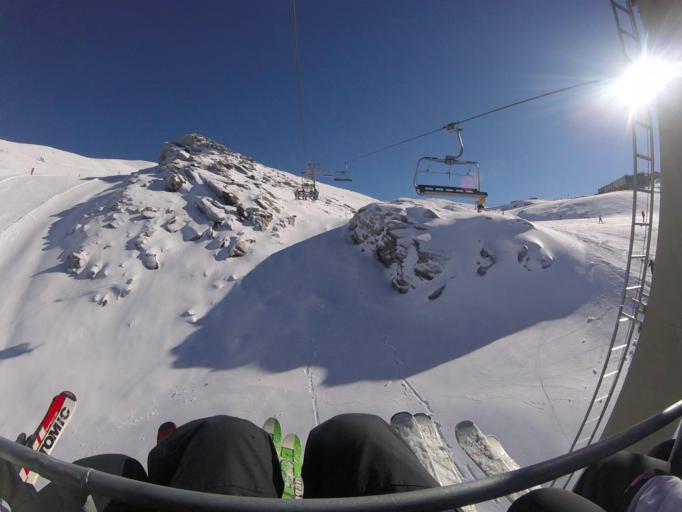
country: ES
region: Andalusia
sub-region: Provincia de Granada
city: Guejar-Sierra
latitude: 37.0752
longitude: -3.3872
